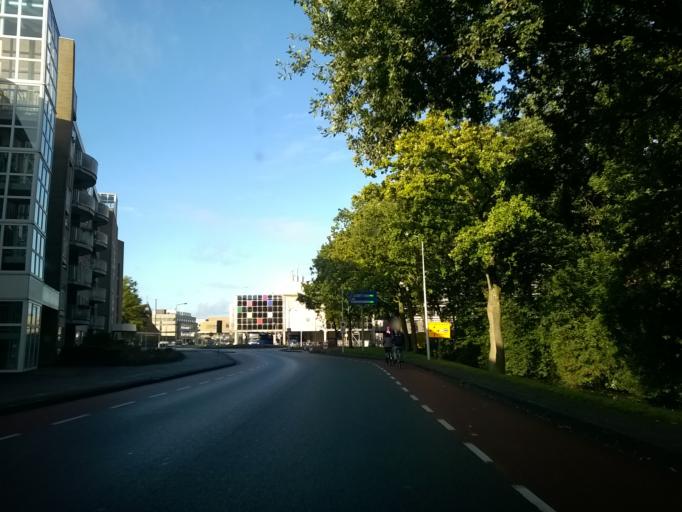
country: NL
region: Friesland
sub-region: Gemeente Smallingerland
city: Drachten
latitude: 53.1039
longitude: 6.1028
